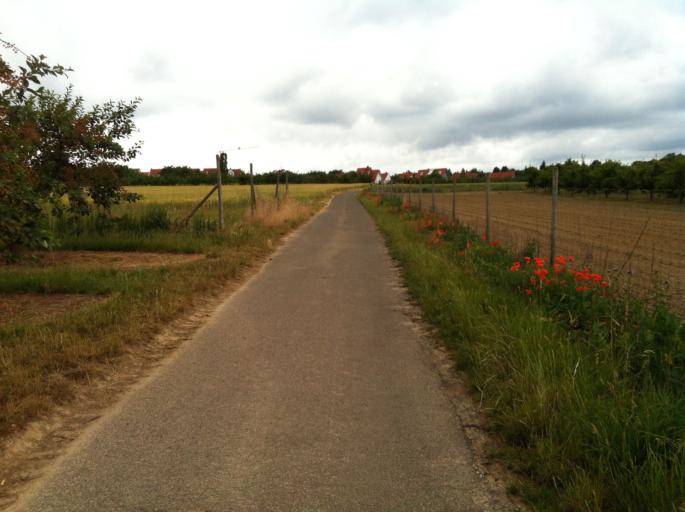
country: DE
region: Rheinland-Pfalz
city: Klein-Winternheim
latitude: 49.9709
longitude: 8.1989
